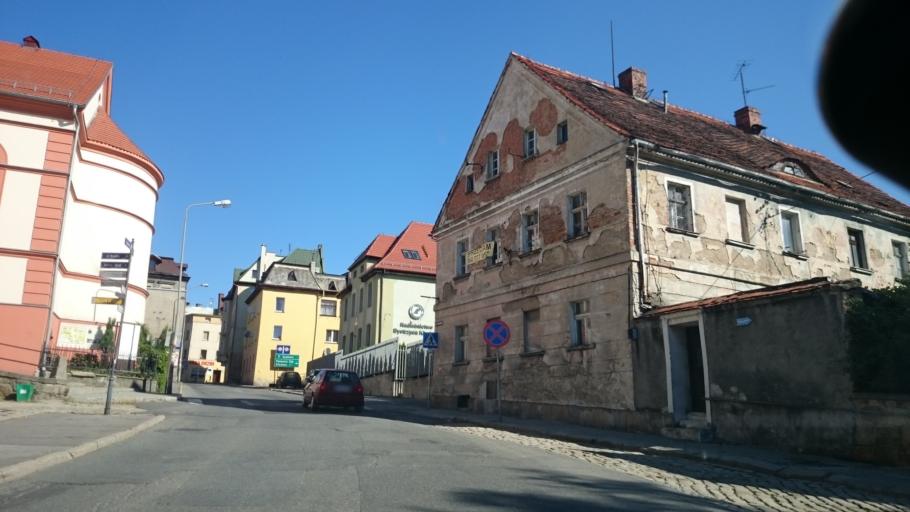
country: PL
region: Lower Silesian Voivodeship
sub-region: Powiat klodzki
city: Bystrzyca Klodzka
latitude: 50.2969
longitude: 16.6543
